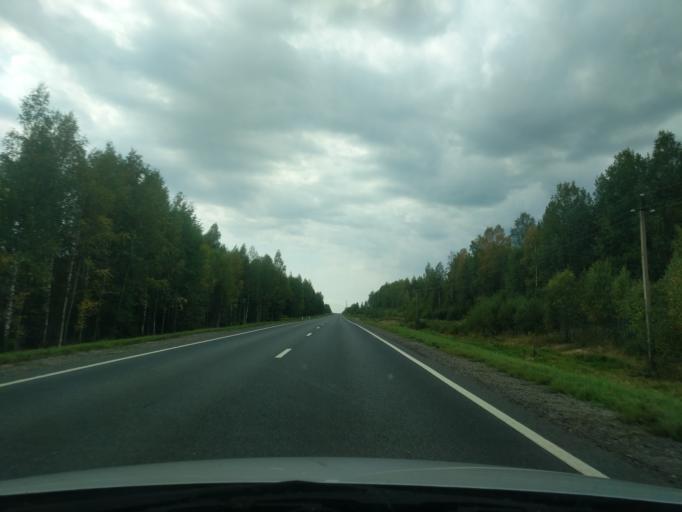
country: RU
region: Kostroma
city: Manturovo
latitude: 58.1519
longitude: 44.3758
